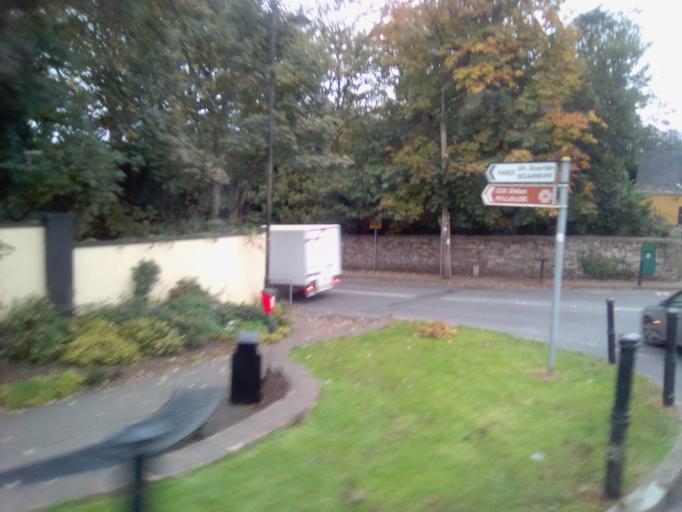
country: IE
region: Munster
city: Ballina
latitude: 52.8090
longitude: -8.4371
